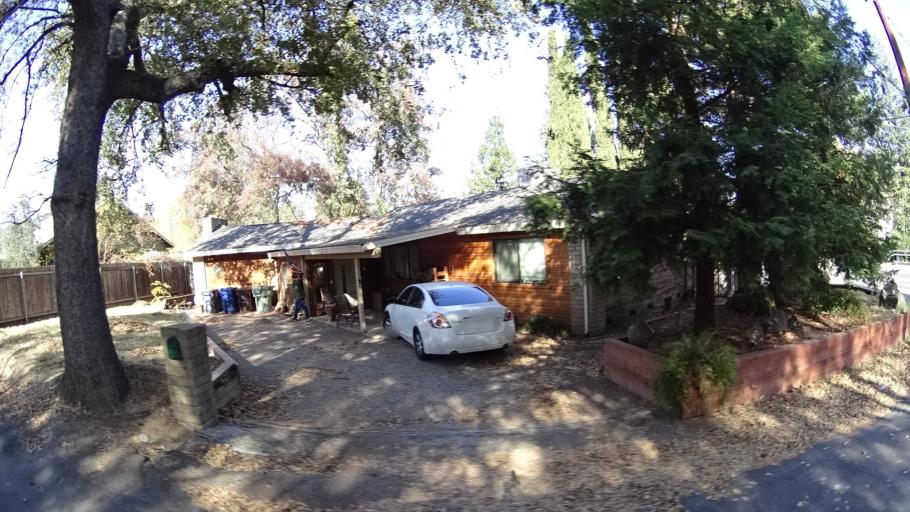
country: US
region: California
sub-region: Sacramento County
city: Citrus Heights
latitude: 38.7021
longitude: -121.2814
